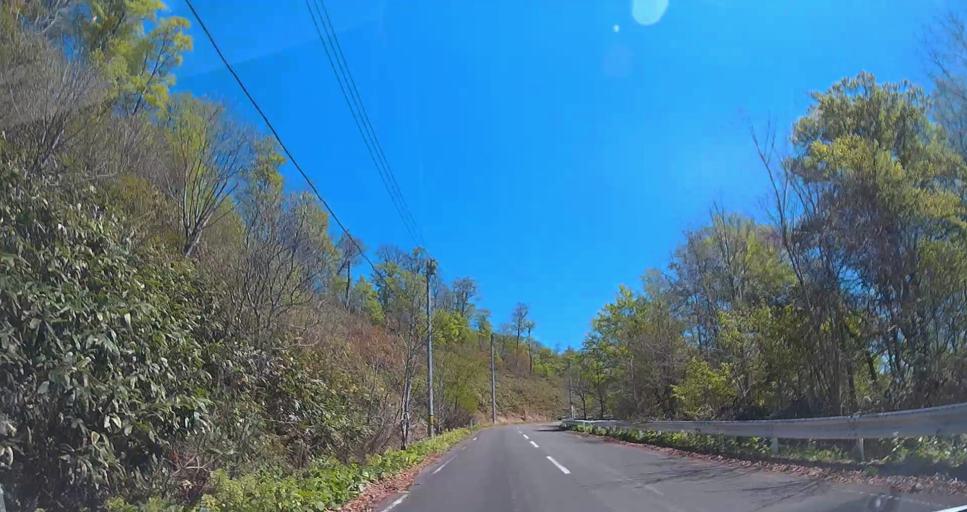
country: JP
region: Aomori
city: Mutsu
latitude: 41.2304
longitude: 140.8115
